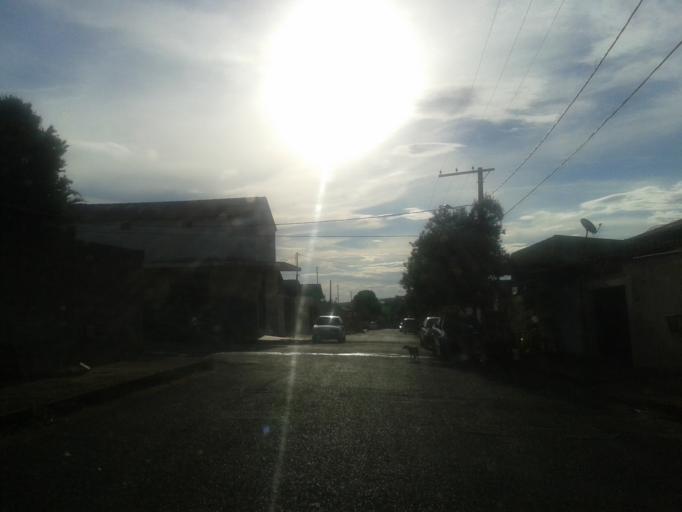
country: BR
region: Minas Gerais
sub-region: Capinopolis
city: Capinopolis
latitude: -18.6793
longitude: -49.5664
